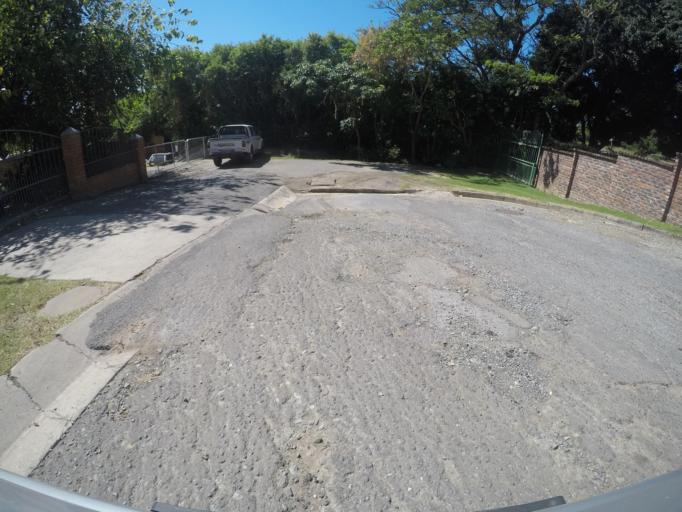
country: ZA
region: Eastern Cape
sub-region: Buffalo City Metropolitan Municipality
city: East London
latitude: -32.9754
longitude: 27.9208
